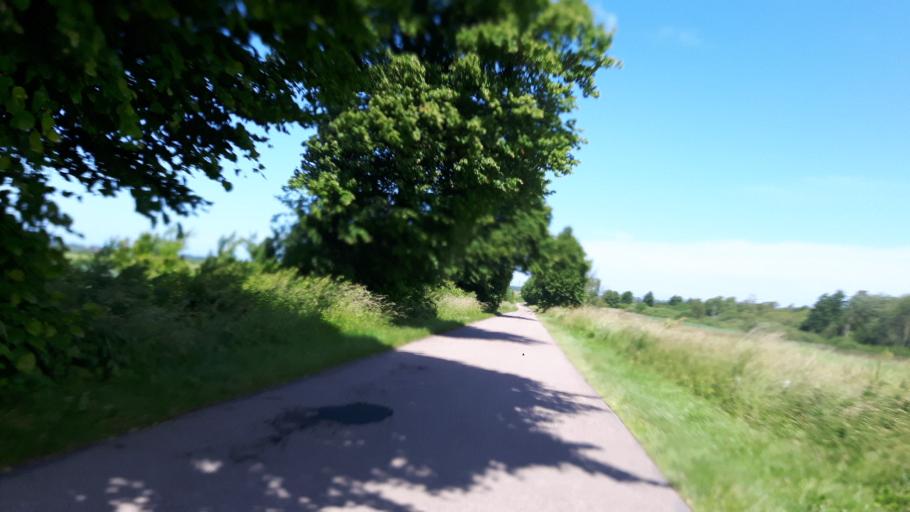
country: PL
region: West Pomeranian Voivodeship
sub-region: Powiat gryficki
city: Mrzezyno
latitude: 54.1082
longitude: 15.3063
